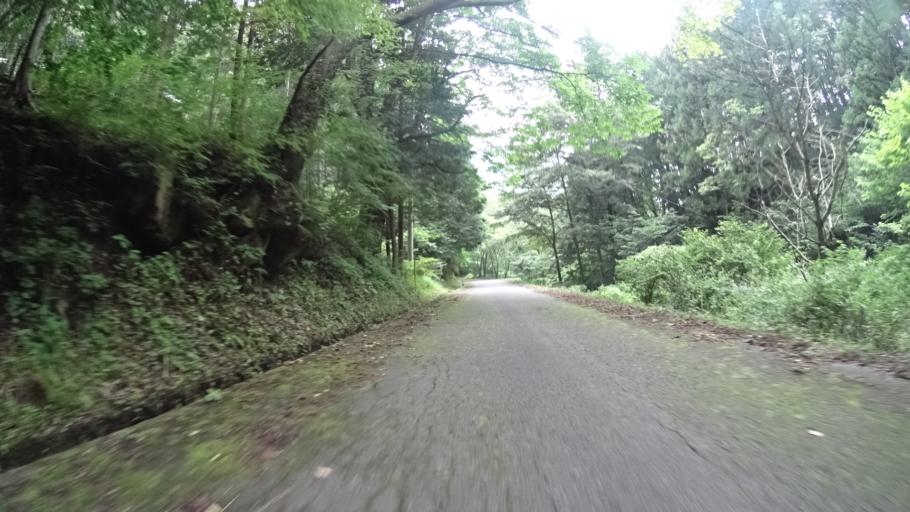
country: JP
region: Yamanashi
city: Kofu-shi
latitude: 35.8080
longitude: 138.5880
